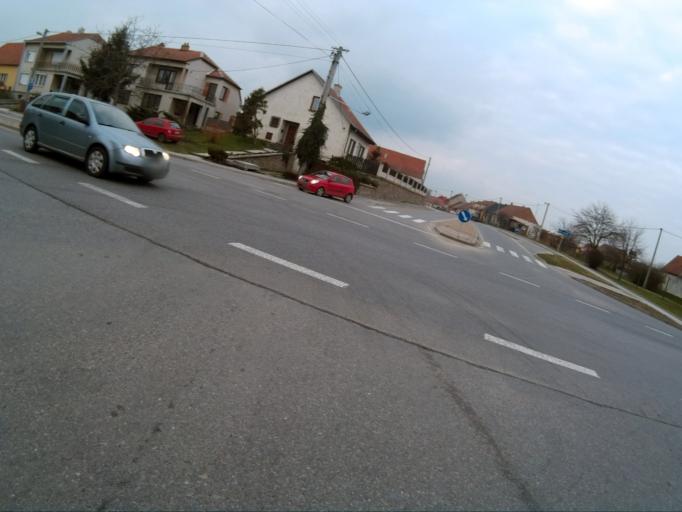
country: CZ
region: South Moravian
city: Velke Nemcice
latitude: 48.9947
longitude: 16.6743
